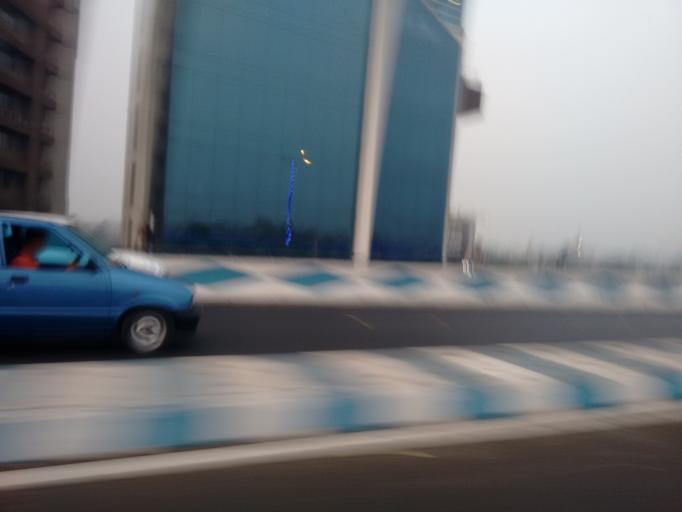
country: IN
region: West Bengal
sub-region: Kolkata
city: Kolkata
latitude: 22.5399
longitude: 88.3806
